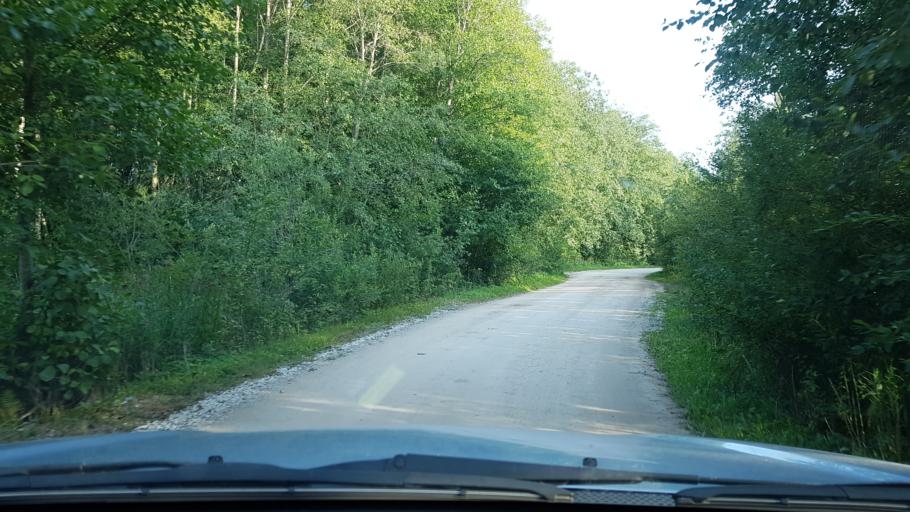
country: EE
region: Ida-Virumaa
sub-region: Sillamaee linn
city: Sillamae
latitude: 59.2729
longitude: 27.9216
